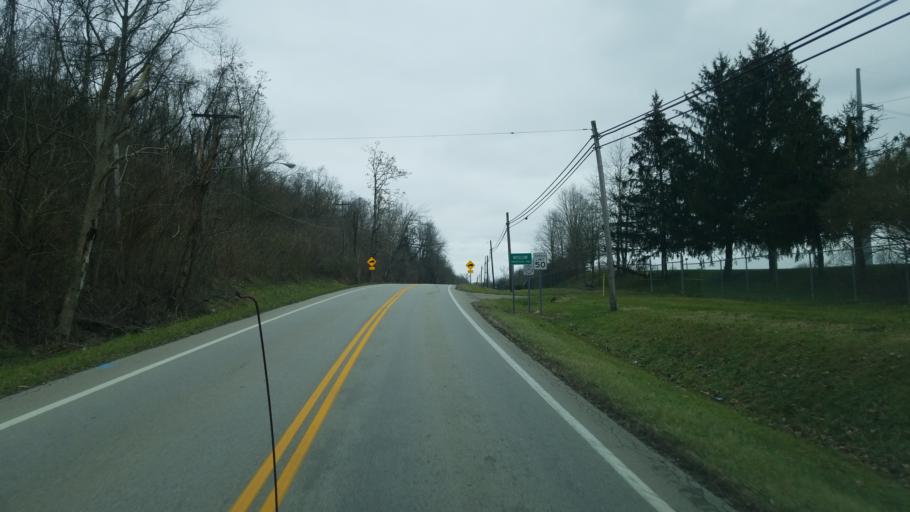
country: US
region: Ohio
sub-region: Clermont County
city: New Richmond
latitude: 38.8658
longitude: -84.2238
